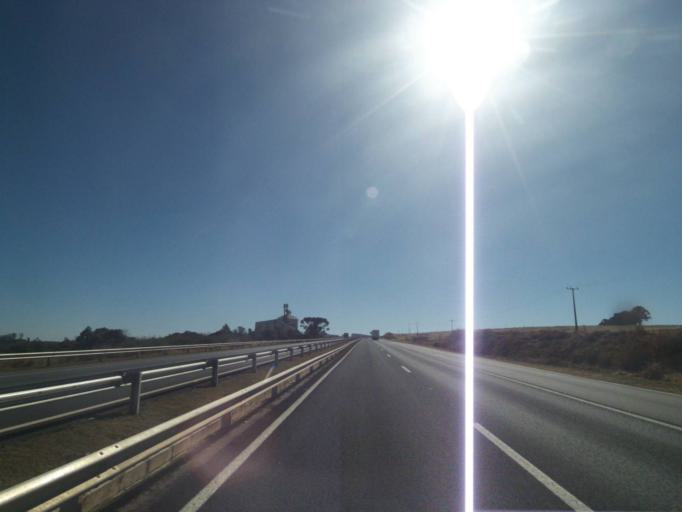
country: BR
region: Parana
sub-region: Tibagi
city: Tibagi
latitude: -24.8302
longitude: -50.4782
